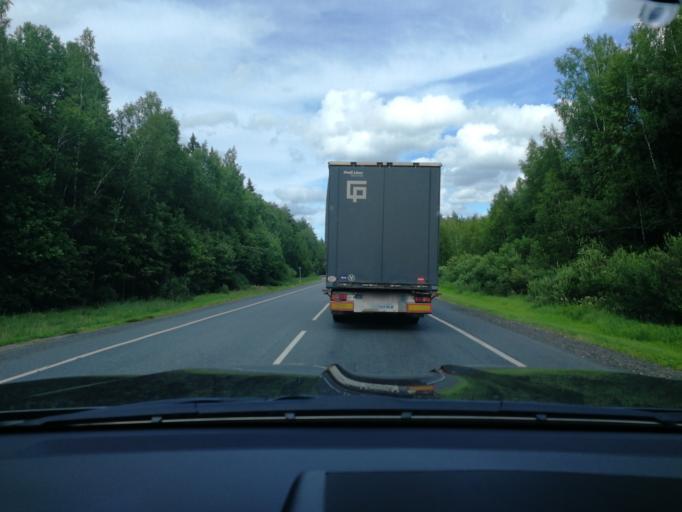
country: RU
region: Moskovskaya
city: Popovo
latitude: 55.0414
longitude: 37.6756
